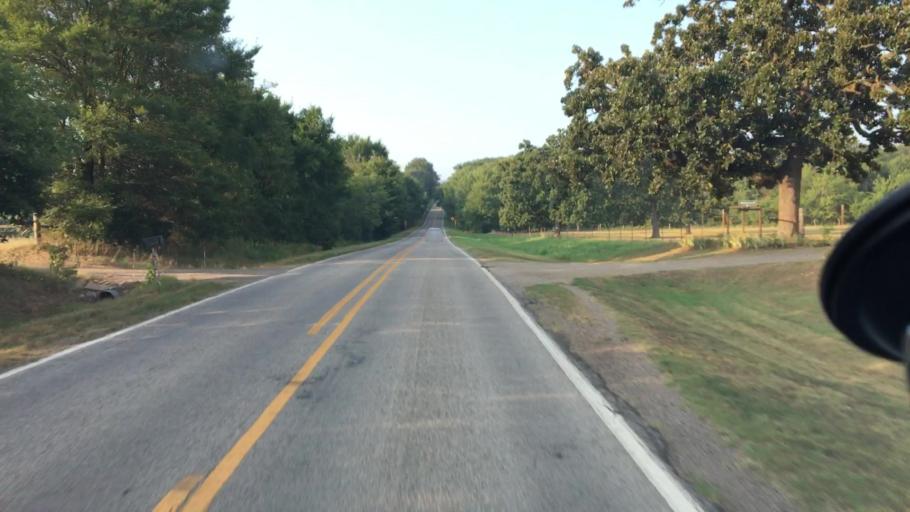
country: US
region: Arkansas
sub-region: Logan County
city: Paris
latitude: 35.3175
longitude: -93.6324
